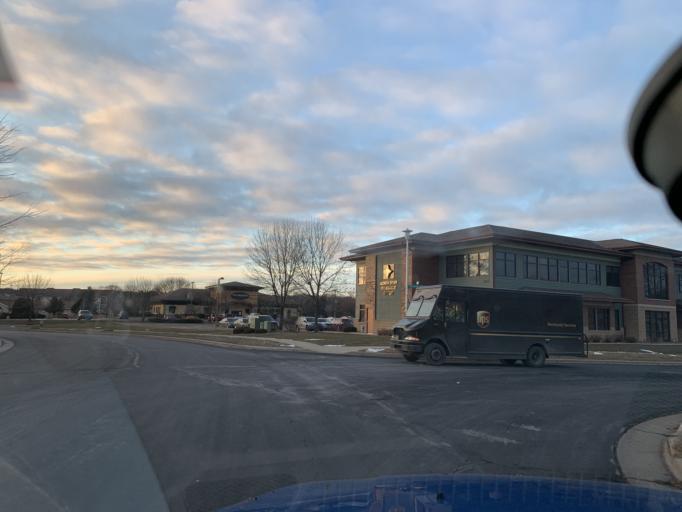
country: US
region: Wisconsin
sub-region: Dane County
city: Madison
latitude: 43.0142
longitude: -89.4285
